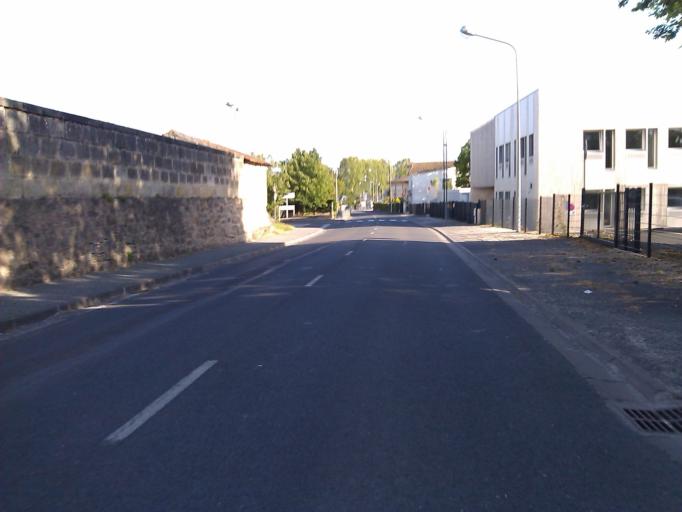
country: FR
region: Aquitaine
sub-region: Departement de la Gironde
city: Cubzac-les-Ponts
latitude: 44.9902
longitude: -0.4509
